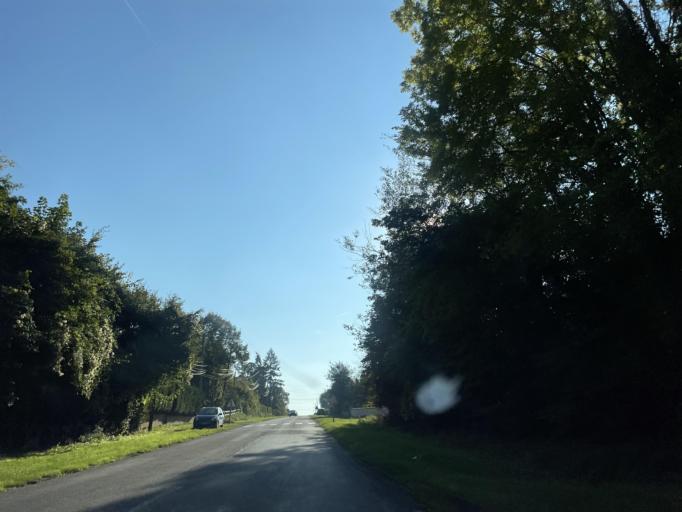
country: FR
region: Ile-de-France
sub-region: Departement de Seine-et-Marne
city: Voulangis
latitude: 48.8472
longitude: 2.8952
